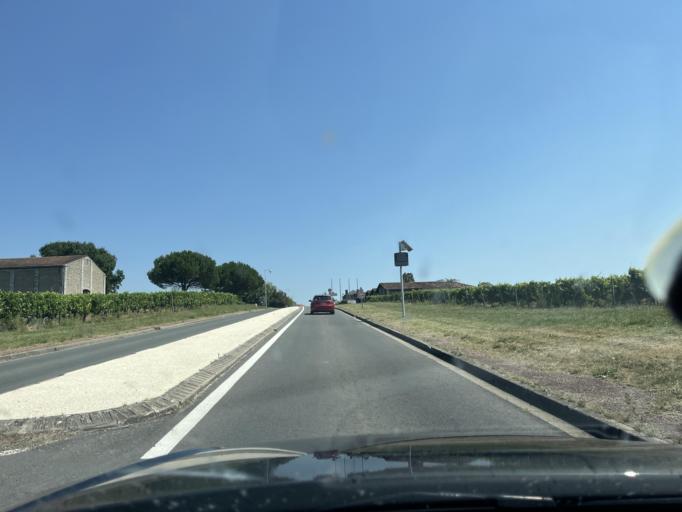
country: FR
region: Poitou-Charentes
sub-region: Departement de la Charente-Maritime
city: Mortagne-sur-Gironde
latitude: 45.4593
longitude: -0.6941
